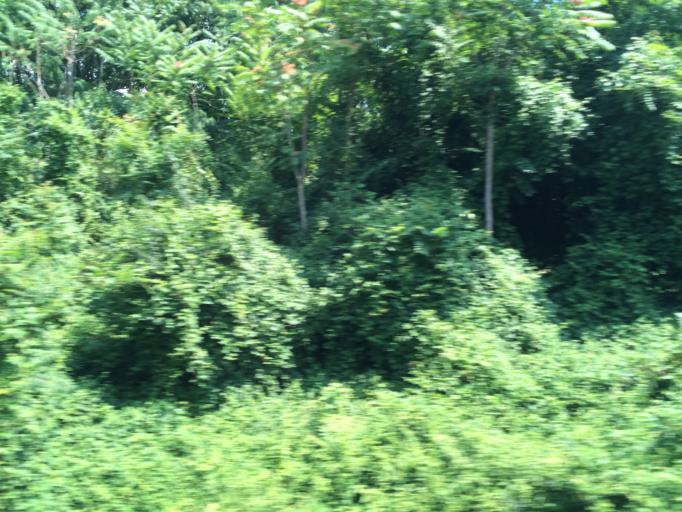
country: US
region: Pennsylvania
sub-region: Delaware County
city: Colwyn
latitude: 39.9261
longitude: -75.2218
